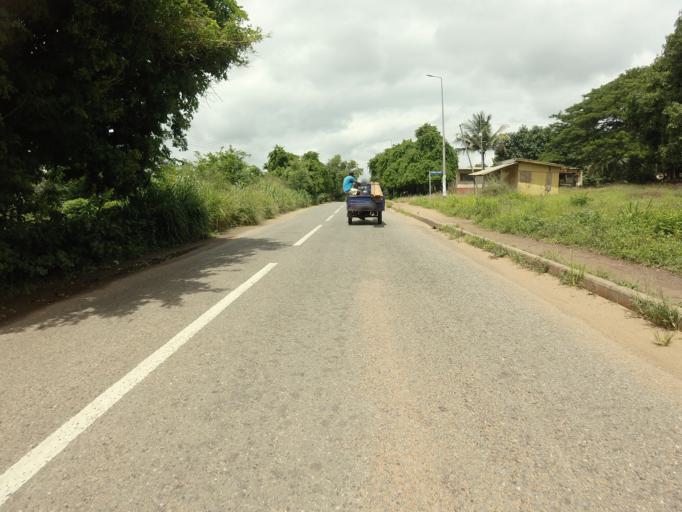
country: GH
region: Volta
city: Ho
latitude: 6.5971
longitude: 0.4799
